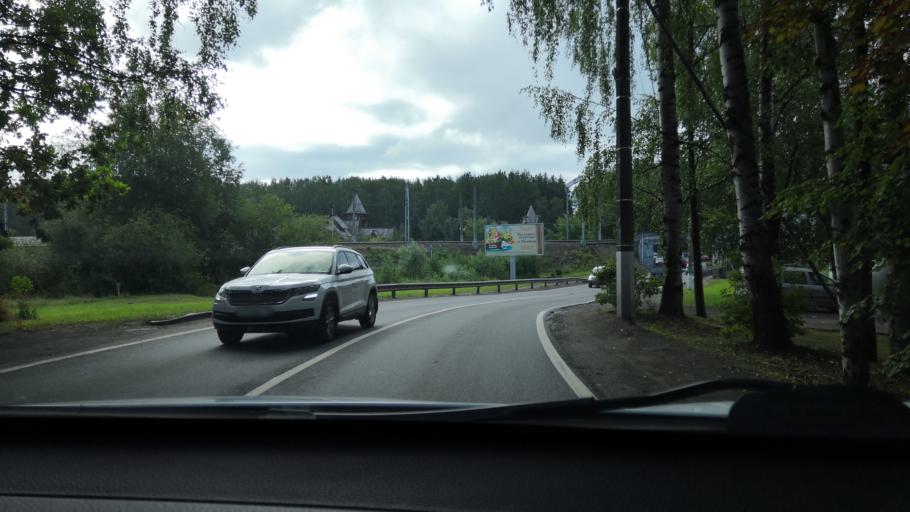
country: RU
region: St.-Petersburg
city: Pavlovsk
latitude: 59.6969
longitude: 30.4355
